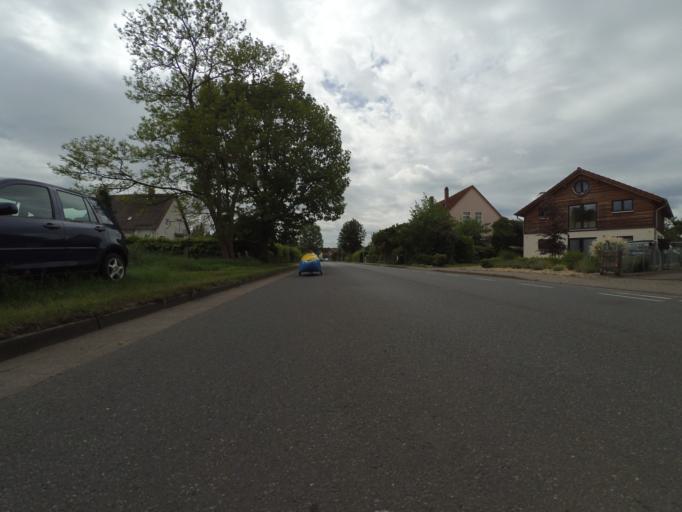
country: DE
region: Lower Saxony
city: Gross Munzel
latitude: 52.4312
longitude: 9.5142
